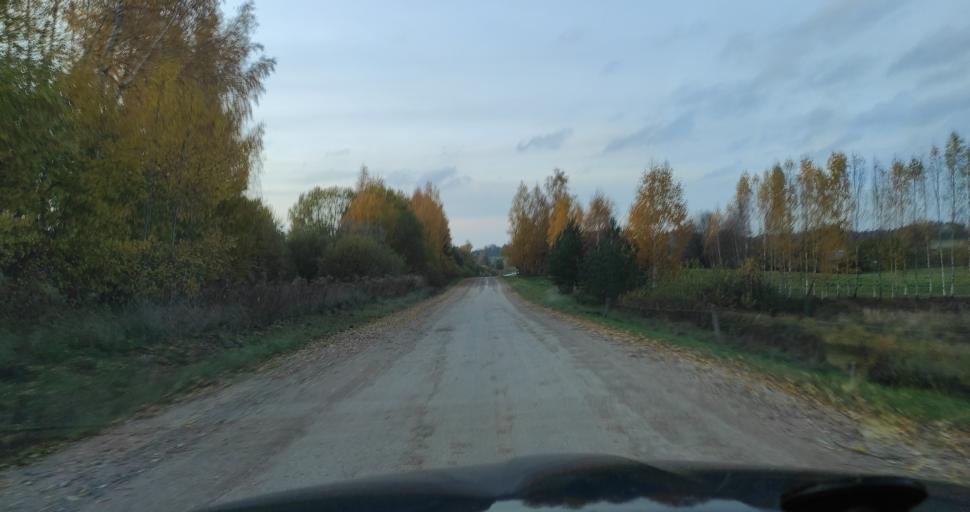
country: LV
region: Aizpute
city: Aizpute
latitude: 56.6446
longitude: 21.8021
